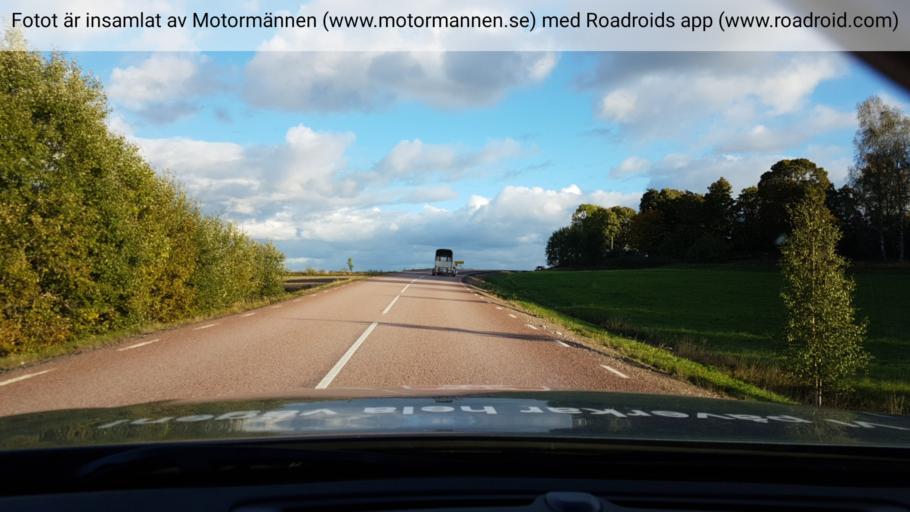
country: SE
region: Vaermland
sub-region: Karlstads Kommun
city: Molkom
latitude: 59.5588
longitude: 13.7761
